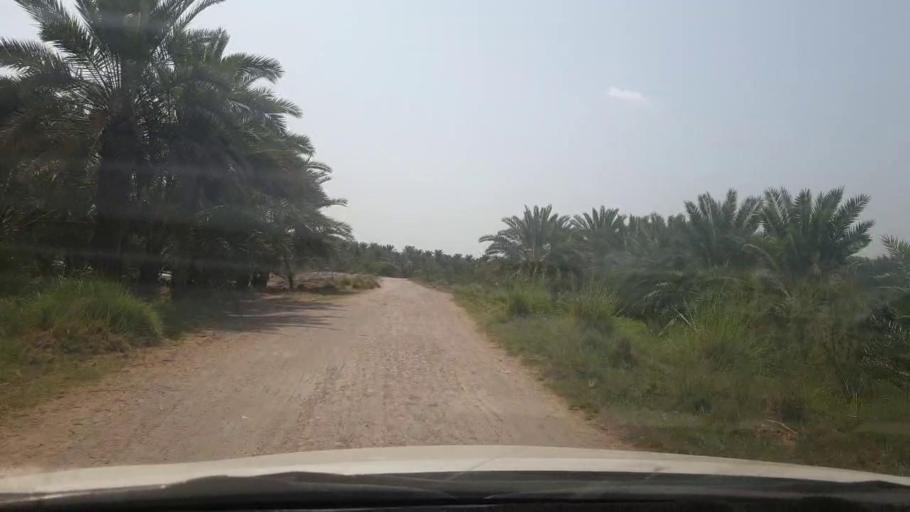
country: PK
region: Sindh
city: Khairpur
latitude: 27.5578
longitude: 68.8536
